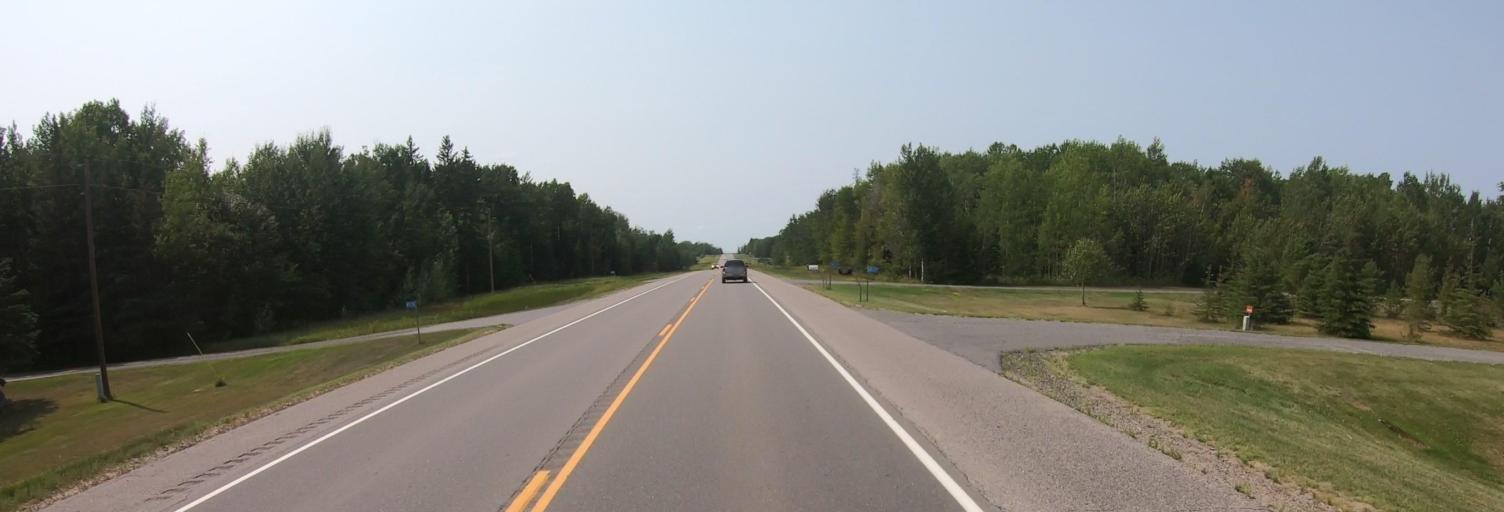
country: US
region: Minnesota
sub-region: Koochiching County
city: International Falls
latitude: 48.5434
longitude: -93.4643
